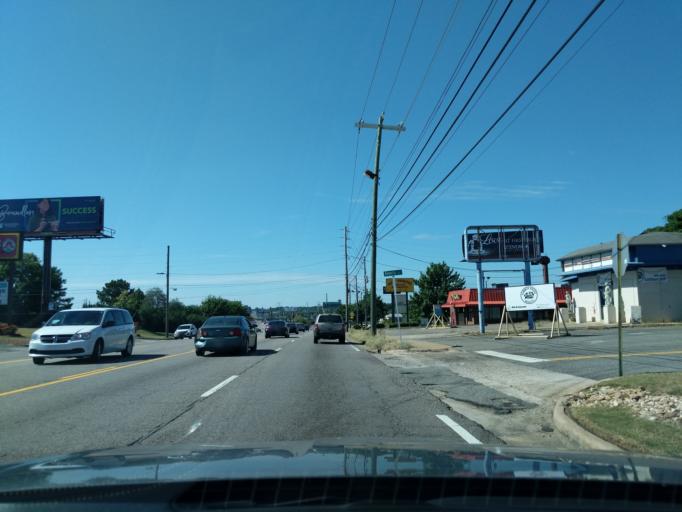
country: US
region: Georgia
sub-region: Columbia County
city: Martinez
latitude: 33.5095
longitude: -82.0261
